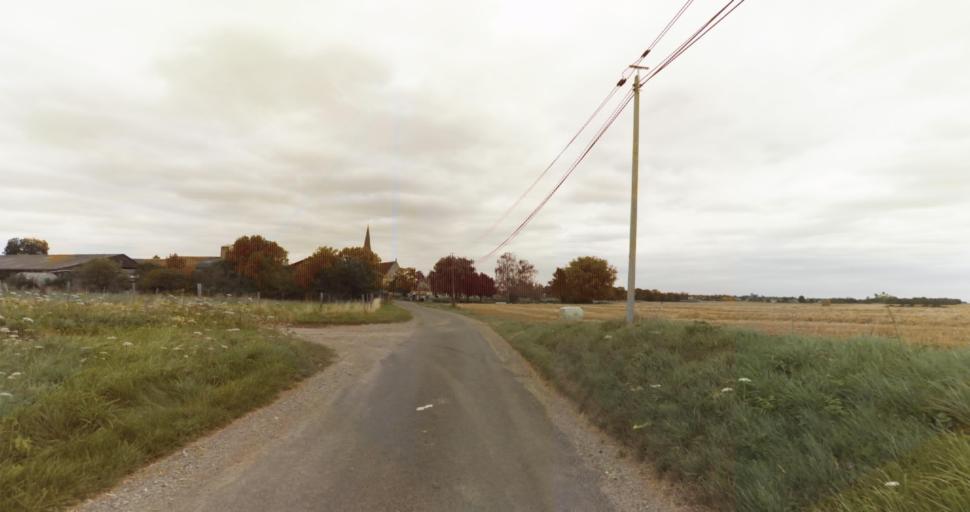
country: FR
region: Haute-Normandie
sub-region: Departement de l'Eure
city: Menilles
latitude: 48.9585
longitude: 1.2876
